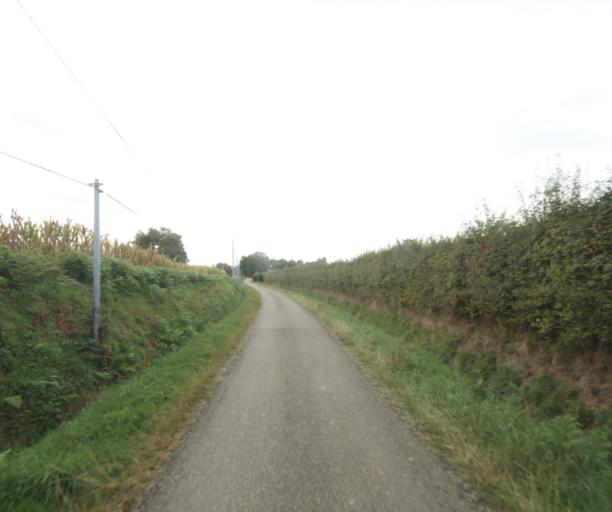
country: FR
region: Midi-Pyrenees
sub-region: Departement du Gers
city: Cazaubon
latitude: 43.8552
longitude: -0.1100
